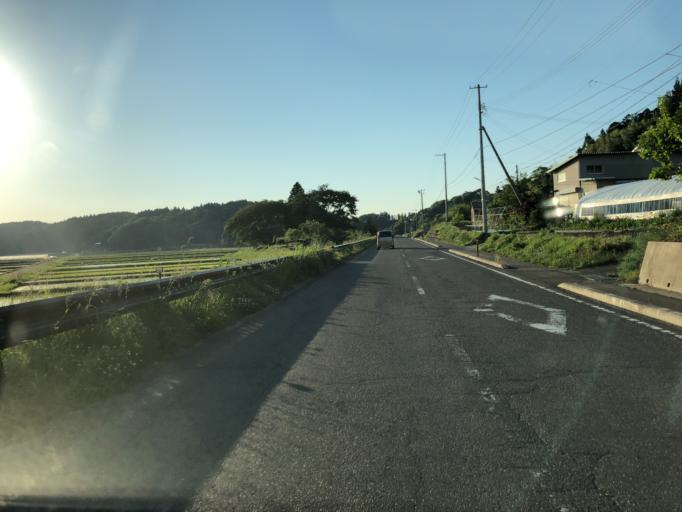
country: JP
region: Fukushima
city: Ishikawa
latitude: 37.0890
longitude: 140.4140
